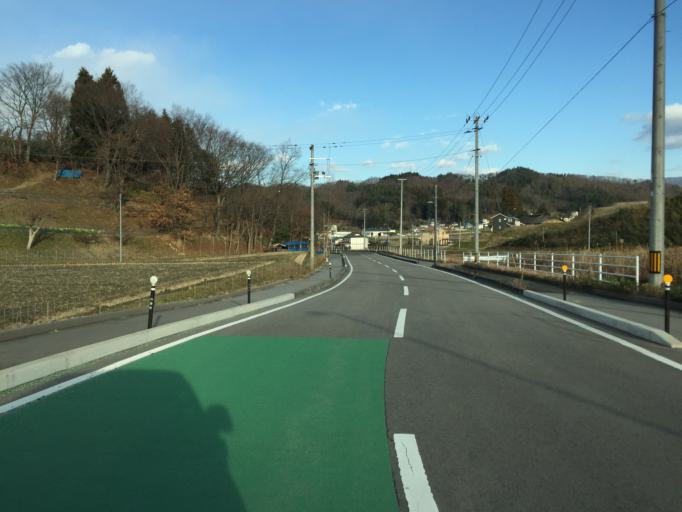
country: JP
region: Fukushima
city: Fukushima-shi
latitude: 37.6692
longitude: 140.5621
